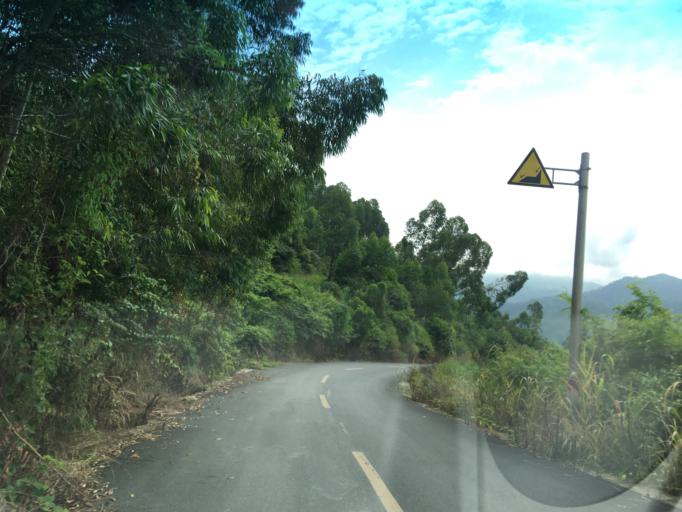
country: CN
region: Guangxi Zhuangzu Zizhiqu
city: Xinzhou
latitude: 24.8191
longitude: 105.6433
